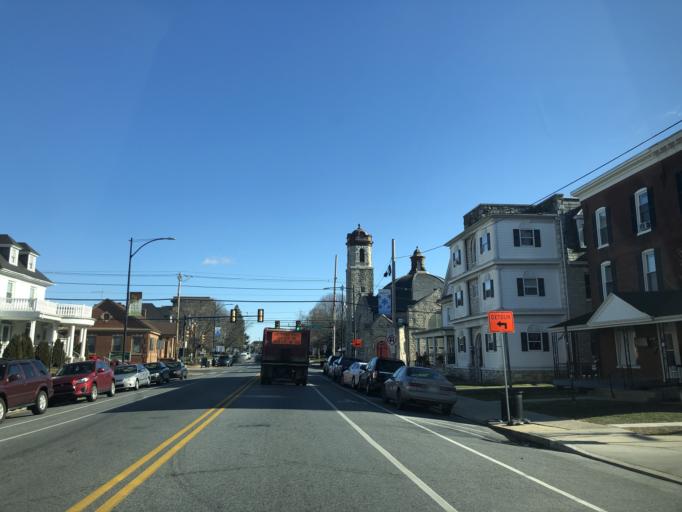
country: US
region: Pennsylvania
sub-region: Chester County
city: Coatesville
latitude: 39.9853
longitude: -75.8121
